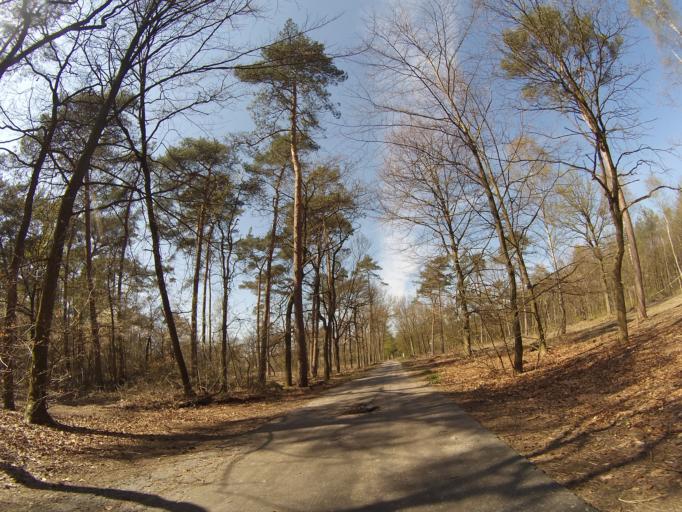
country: NL
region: Utrecht
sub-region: Gemeente Utrechtse Heuvelrug
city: Driebergen-Rijsenburg
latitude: 52.0948
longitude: 5.2979
